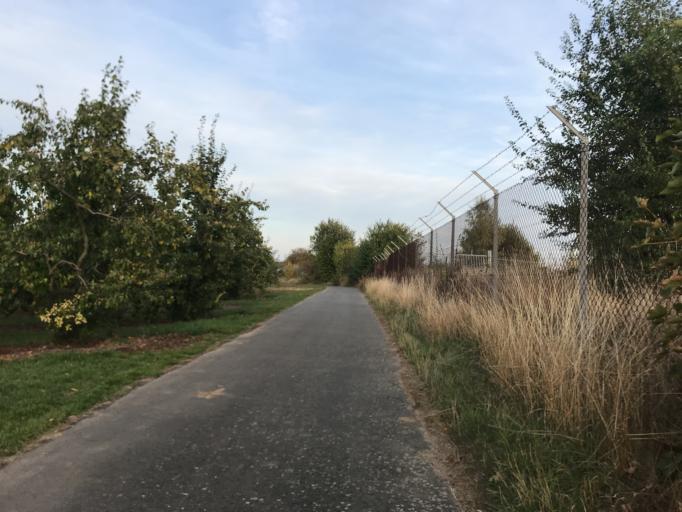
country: DE
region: Rheinland-Pfalz
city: Wackernheim
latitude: 49.9715
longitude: 8.1551
